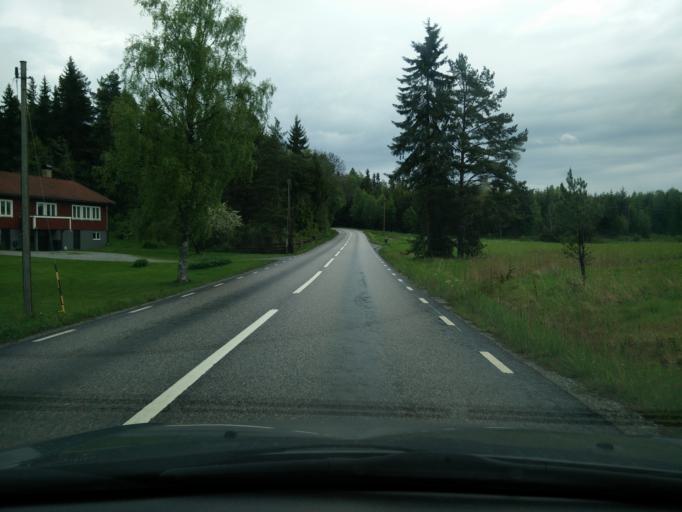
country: SE
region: Stockholm
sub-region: Norrtalje Kommun
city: Bjorko
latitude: 59.7958
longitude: 18.8707
